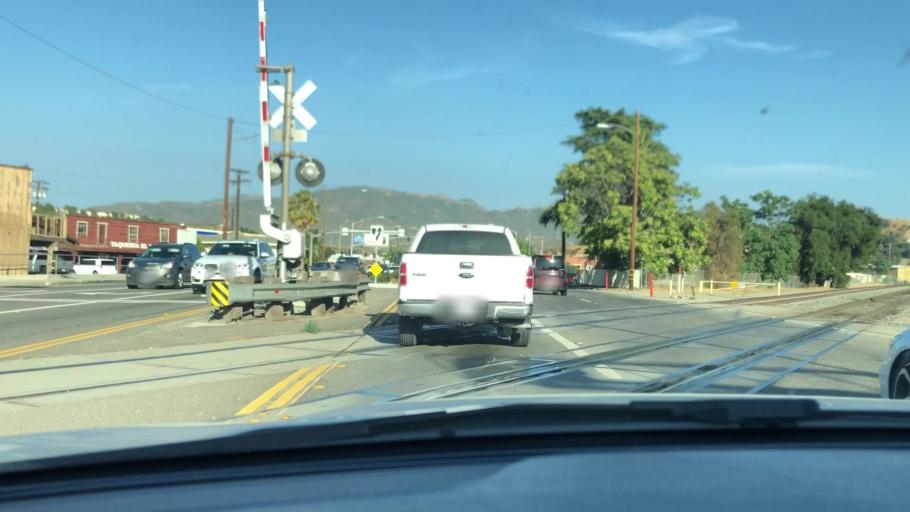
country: US
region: California
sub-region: Los Angeles County
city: Santa Clarita
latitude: 34.3753
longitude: -118.5237
